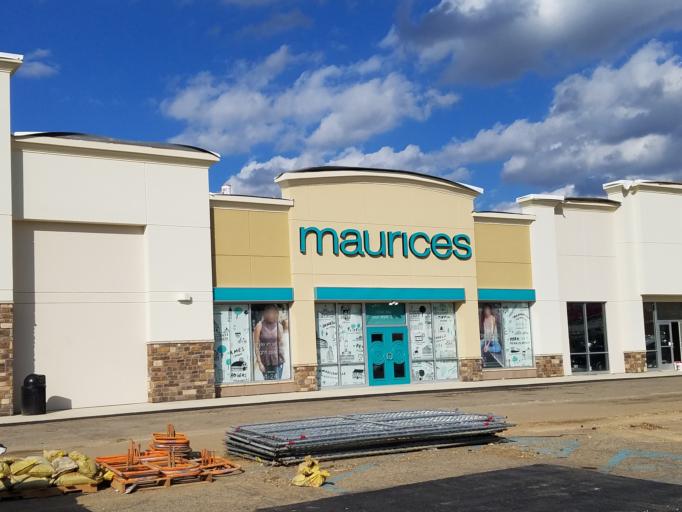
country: US
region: Ohio
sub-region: Knox County
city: Mount Vernon
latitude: 40.4002
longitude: -82.4564
